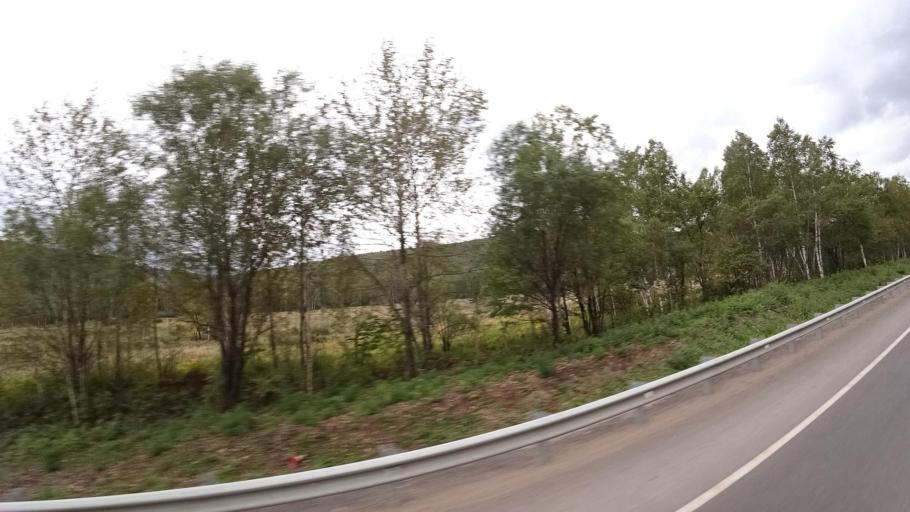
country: RU
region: Jewish Autonomous Oblast
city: Khingansk
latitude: 48.9838
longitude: 131.1459
